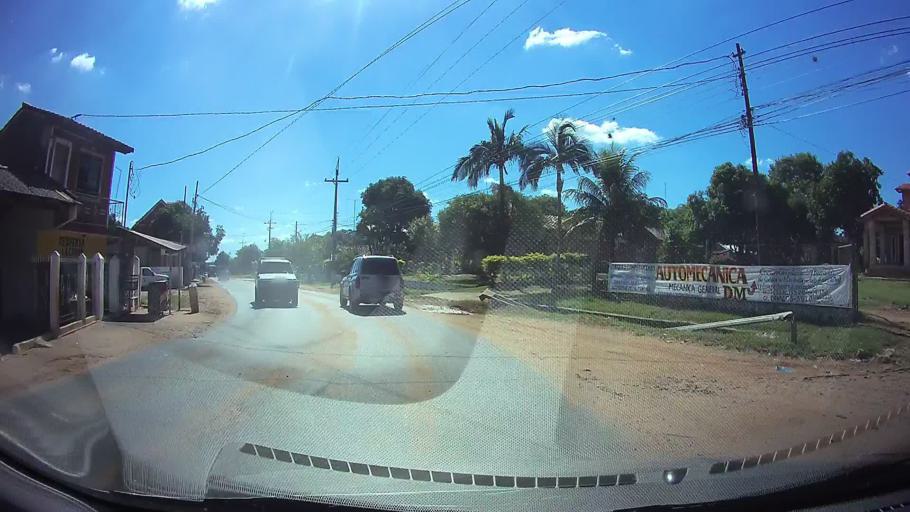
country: PY
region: Central
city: Limpio
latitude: -25.2058
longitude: -57.4623
